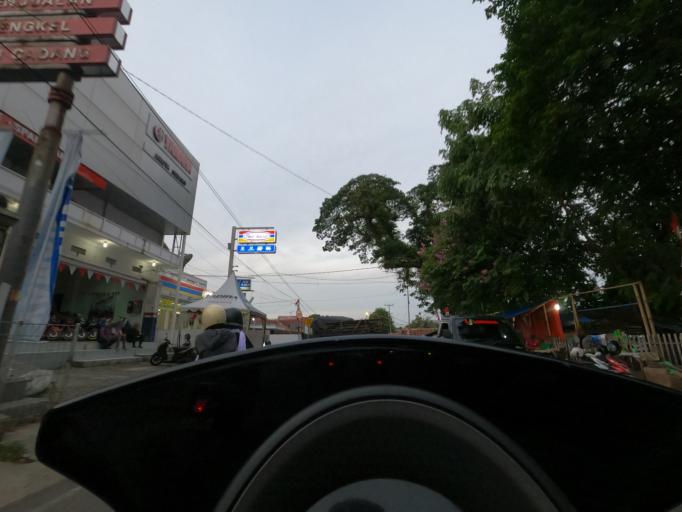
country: ID
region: West Java
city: Lembang
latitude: -6.5739
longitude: 107.7573
